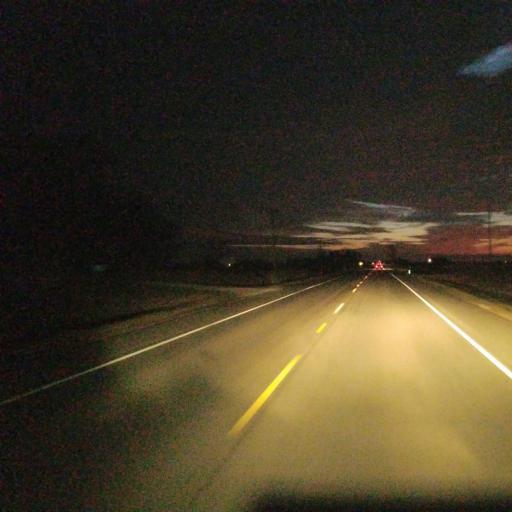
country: US
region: Illinois
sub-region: Fulton County
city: Farmington
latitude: 40.6983
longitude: -89.9401
